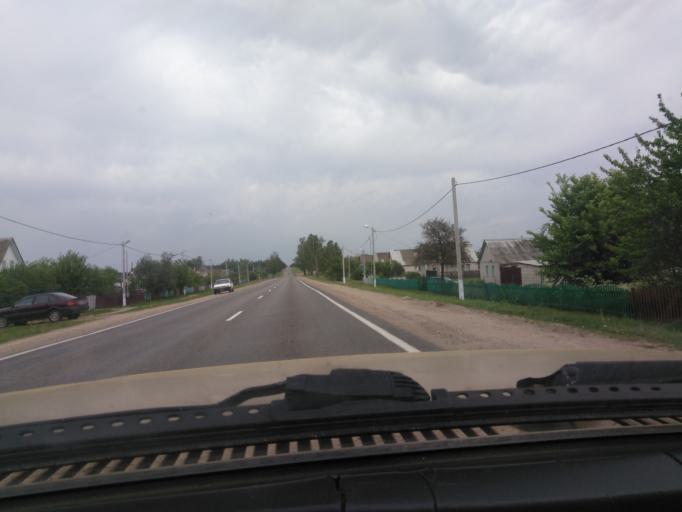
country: BY
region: Mogilev
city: Palykavichy Pyershyya
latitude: 54.0263
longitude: 30.3229
